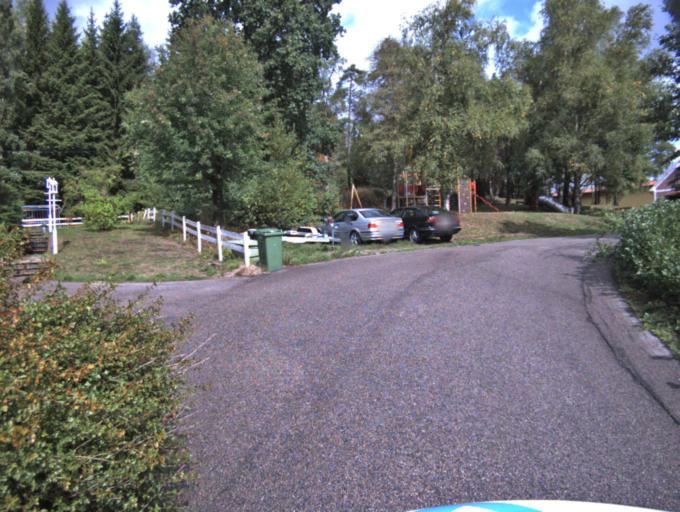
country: SE
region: Vaestra Goetaland
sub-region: Ulricehamns Kommun
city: Ulricehamn
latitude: 57.7267
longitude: 13.3084
